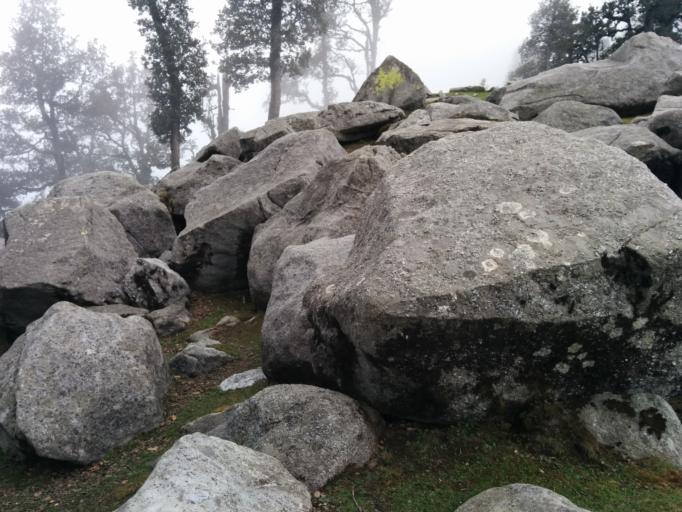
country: IN
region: Himachal Pradesh
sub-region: Kangra
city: Dharmsala
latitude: 32.2774
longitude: 76.3625
